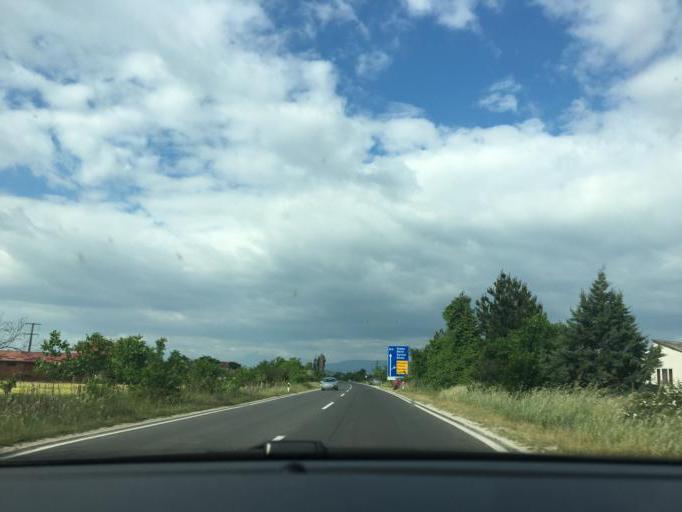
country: MK
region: Prilep
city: Prilep
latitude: 41.3206
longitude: 21.5306
